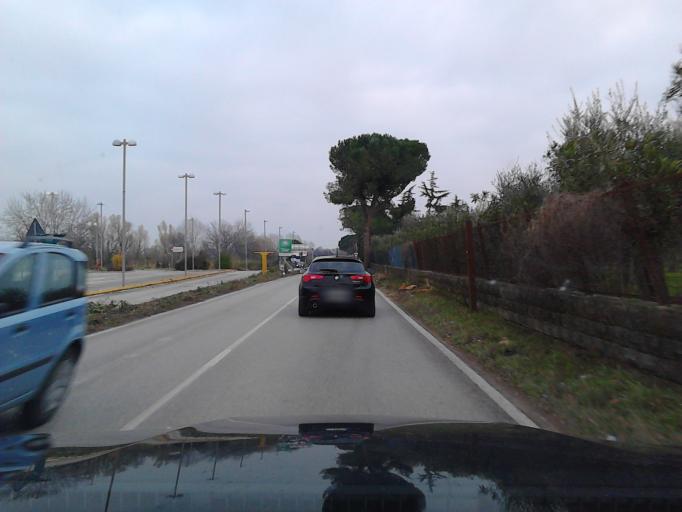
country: IT
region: Abruzzo
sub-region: Provincia di Teramo
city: Alba Adriatica
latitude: 42.8333
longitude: 13.8992
